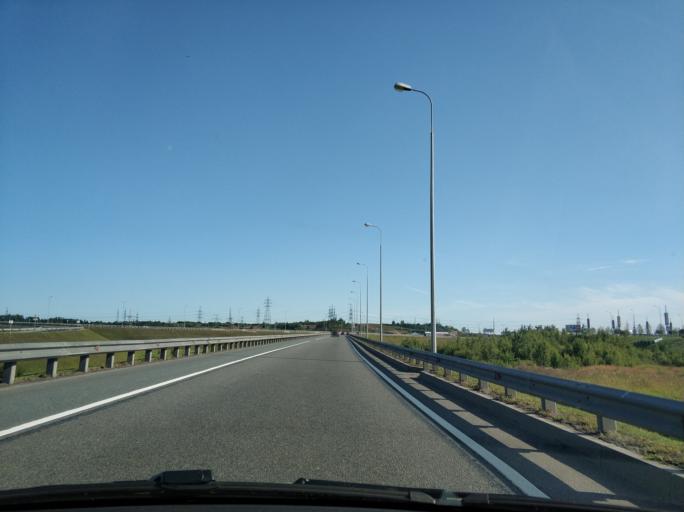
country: RU
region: Leningrad
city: Bugry
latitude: 60.0907
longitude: 30.3725
